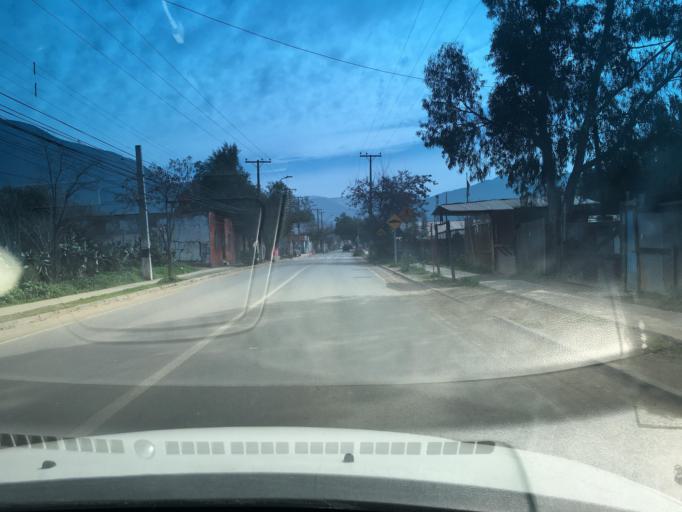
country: CL
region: Santiago Metropolitan
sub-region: Provincia de Chacabuco
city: Lampa
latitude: -33.0875
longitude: -70.9290
